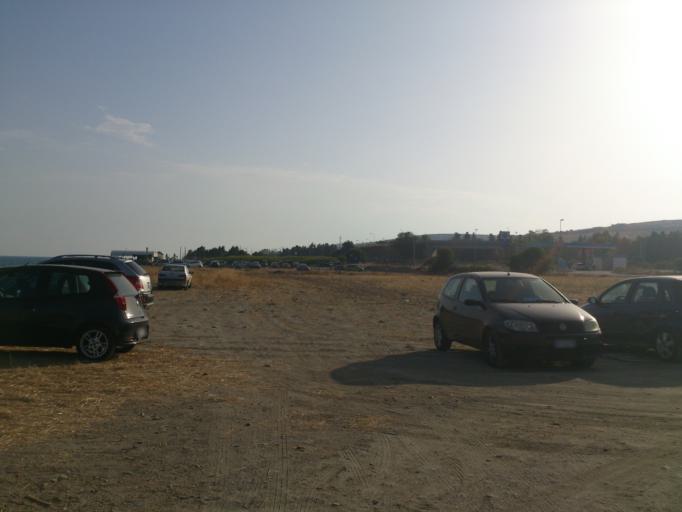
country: IT
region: Calabria
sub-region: Provincia di Reggio Calabria
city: Monasterace Marina
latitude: 38.4199
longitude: 16.5641
